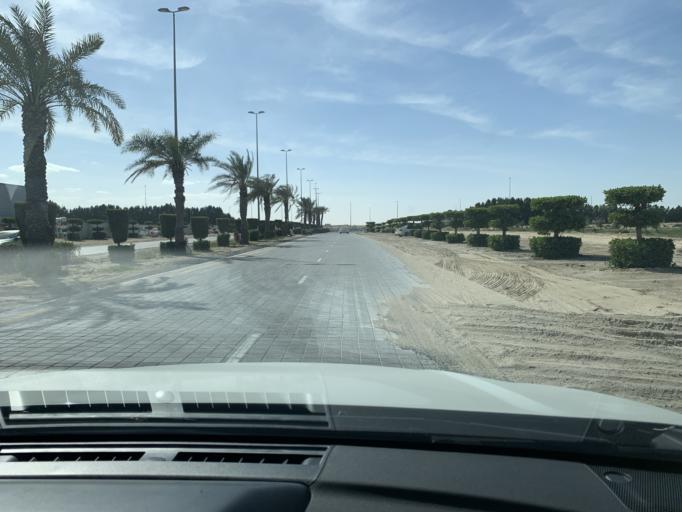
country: AE
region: Dubai
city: Dubai
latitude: 24.9637
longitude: 55.1976
